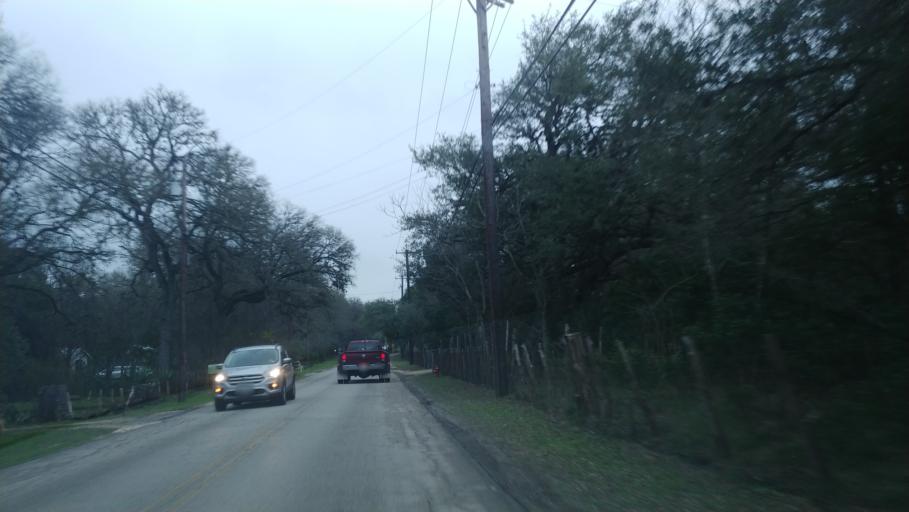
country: US
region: Texas
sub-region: Bexar County
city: Cross Mountain
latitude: 29.6189
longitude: -98.6853
